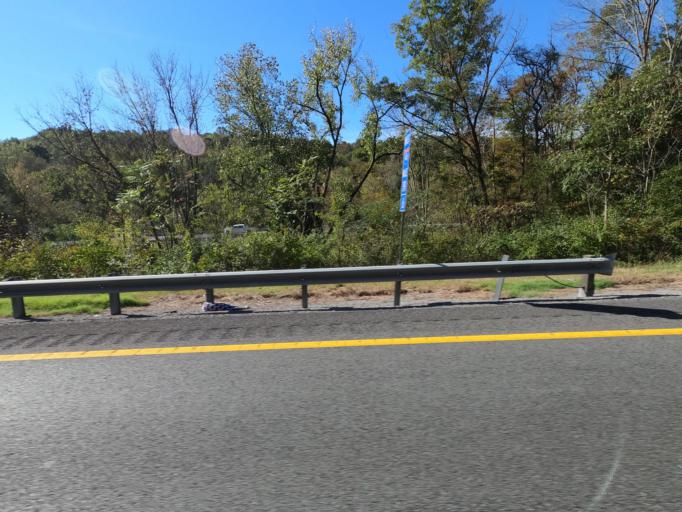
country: US
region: Tennessee
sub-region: Cheatham County
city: Pegram
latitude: 36.0784
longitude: -87.0356
